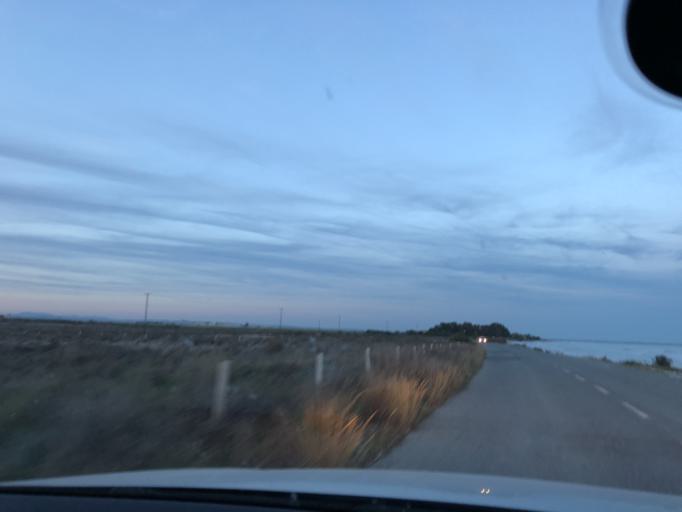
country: CY
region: Larnaka
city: Meneou
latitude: 34.8548
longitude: 33.6282
